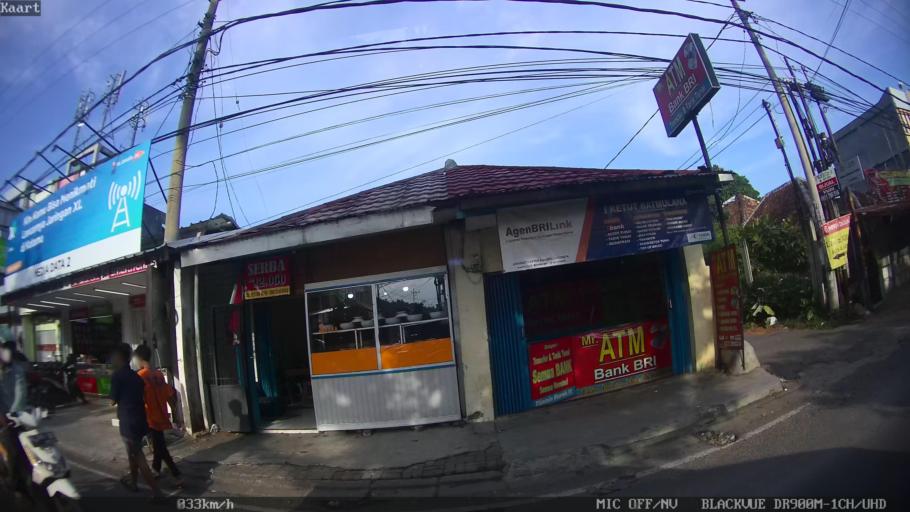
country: ID
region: Lampung
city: Kedaton
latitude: -5.3930
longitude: 105.2620
